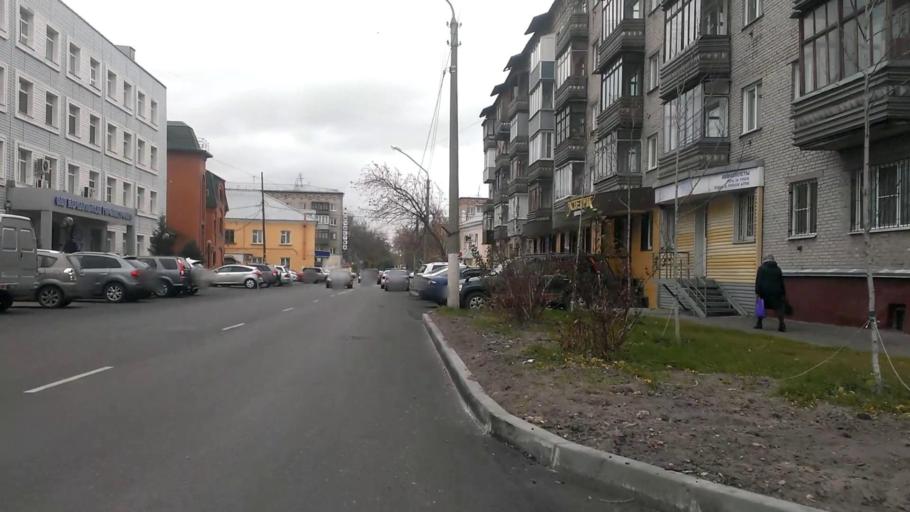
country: RU
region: Altai Krai
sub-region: Gorod Barnaulskiy
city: Barnaul
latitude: 53.3524
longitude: 83.7683
